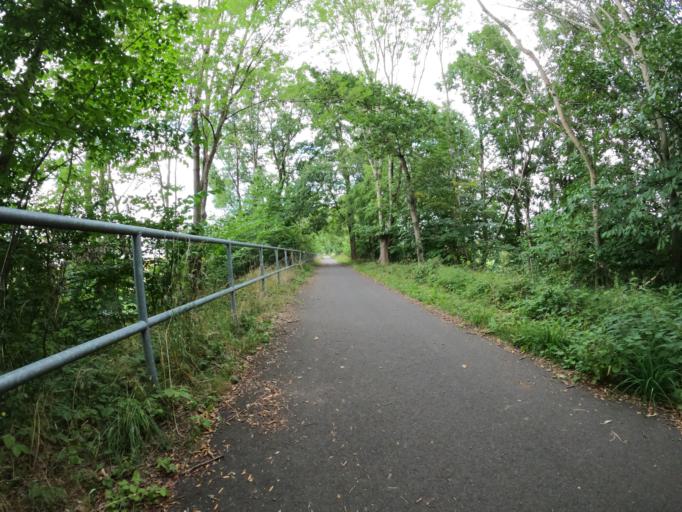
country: DE
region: Mecklenburg-Vorpommern
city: Woldegk
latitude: 53.3618
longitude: 13.5901
